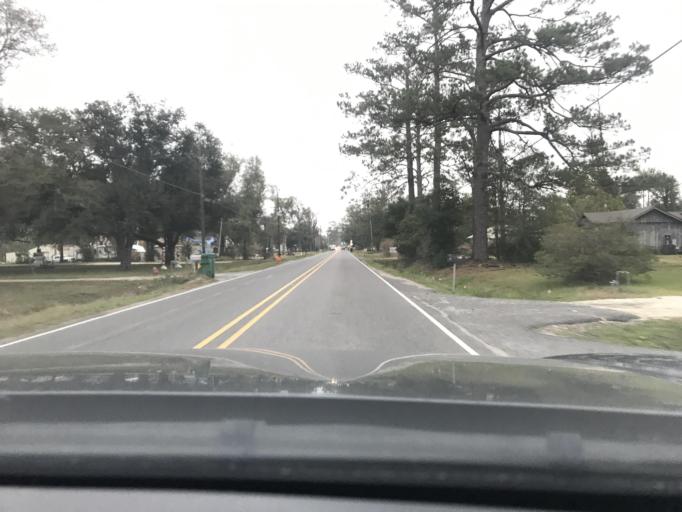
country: US
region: Louisiana
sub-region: Calcasieu Parish
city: Westlake
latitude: 30.2849
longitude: -93.2557
